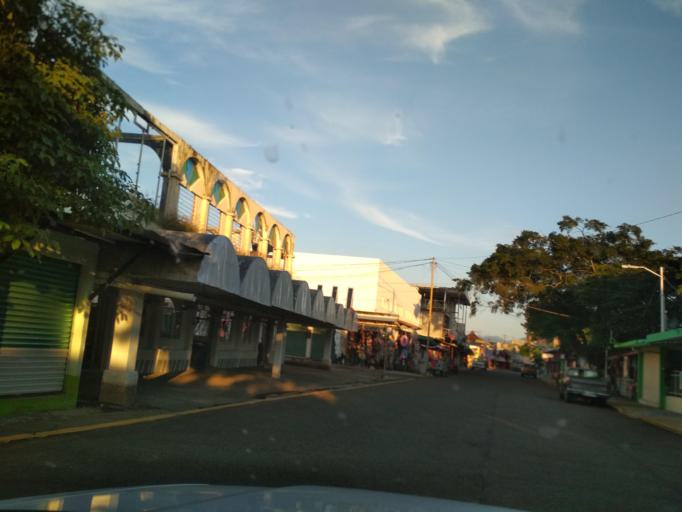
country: MX
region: Veracruz
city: Catemaco
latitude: 18.4175
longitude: -95.1116
